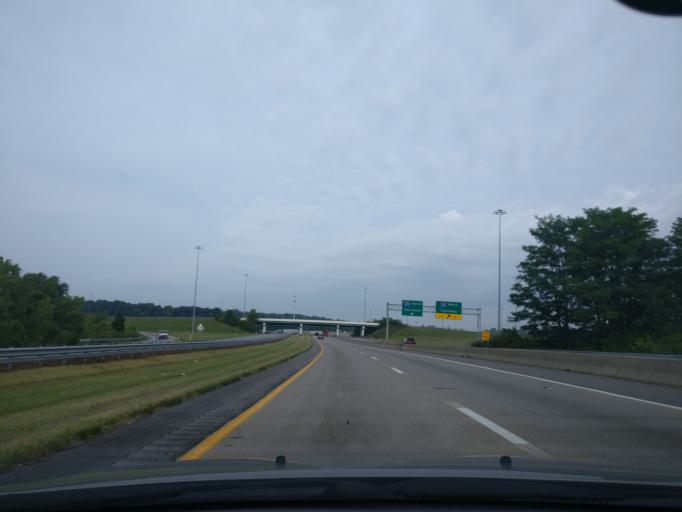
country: US
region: Ohio
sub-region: Greene County
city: Beavercreek
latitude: 39.7351
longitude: -84.0868
